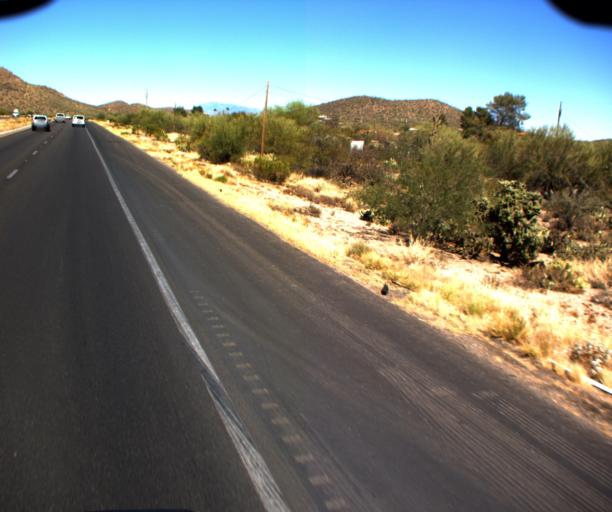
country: US
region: Arizona
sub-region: Pima County
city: Tucson Estates
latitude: 32.1760
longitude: -111.0542
